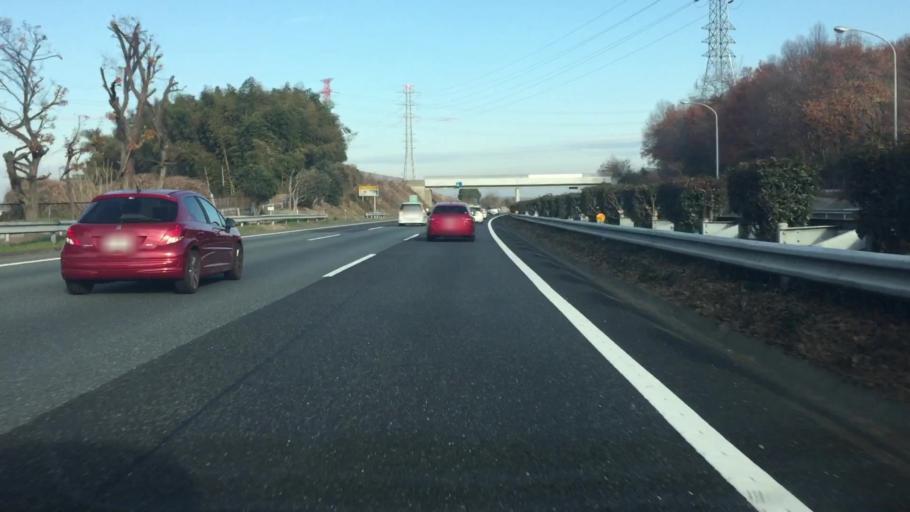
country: JP
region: Saitama
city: Yorii
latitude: 36.1758
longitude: 139.1922
